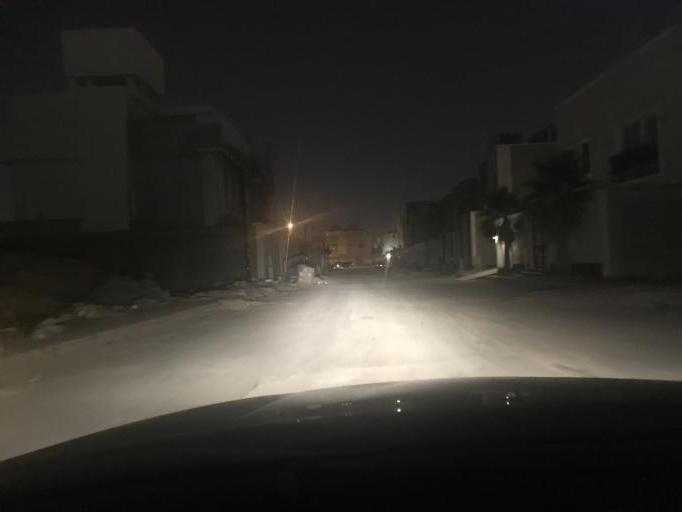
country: SA
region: Ar Riyad
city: Riyadh
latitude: 24.7382
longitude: 46.7853
